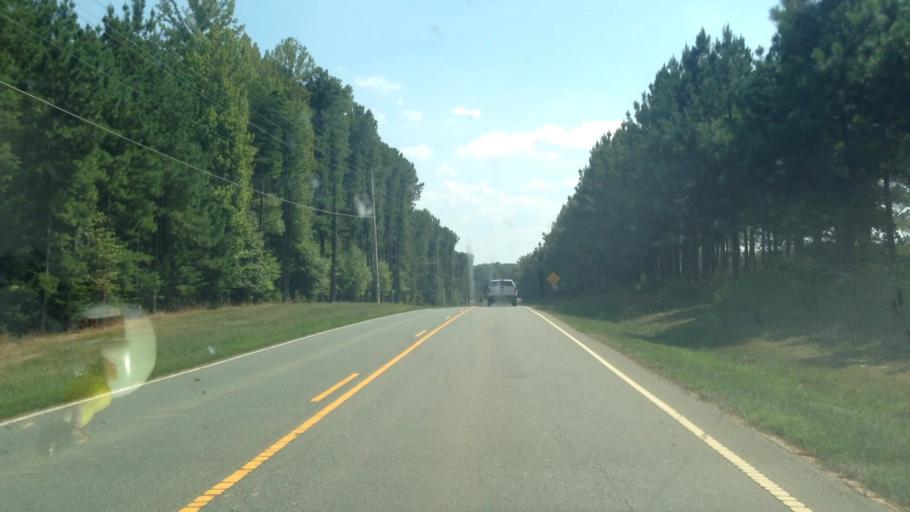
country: US
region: North Carolina
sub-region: Stokes County
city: Walnut Cove
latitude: 36.2931
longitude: -80.0638
